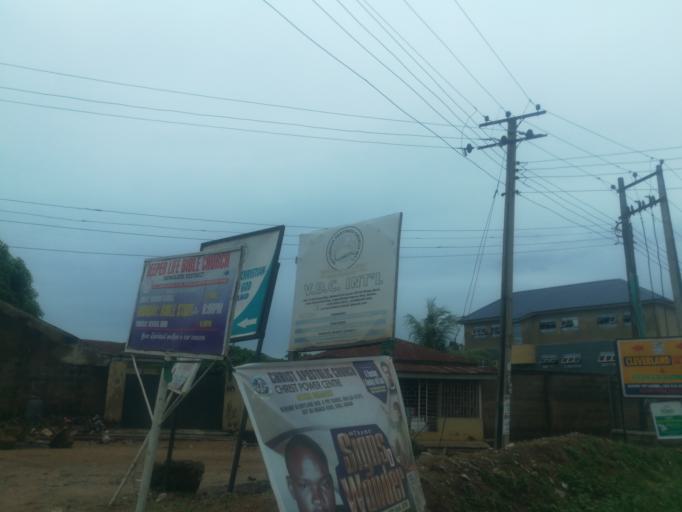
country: NG
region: Oyo
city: Ibadan
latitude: 7.3283
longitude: 3.8921
